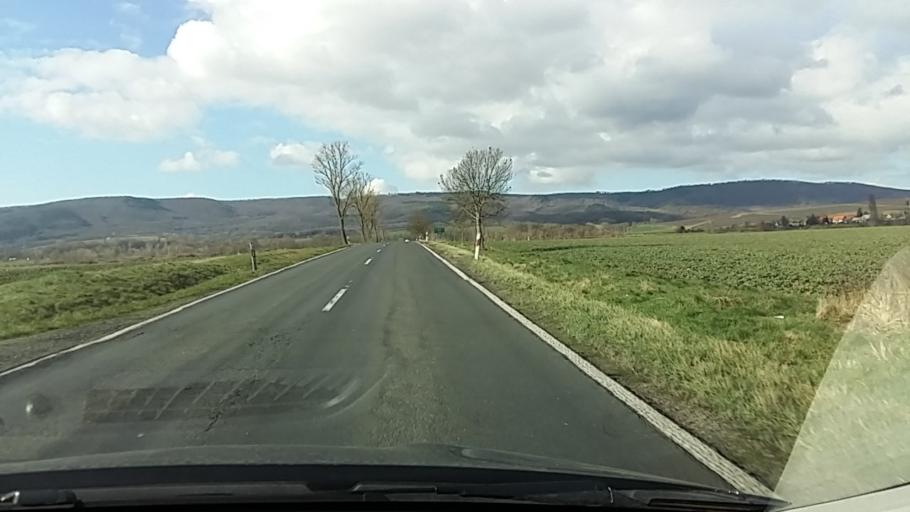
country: HU
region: Veszprem
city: Tapolca
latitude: 46.8490
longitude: 17.3780
